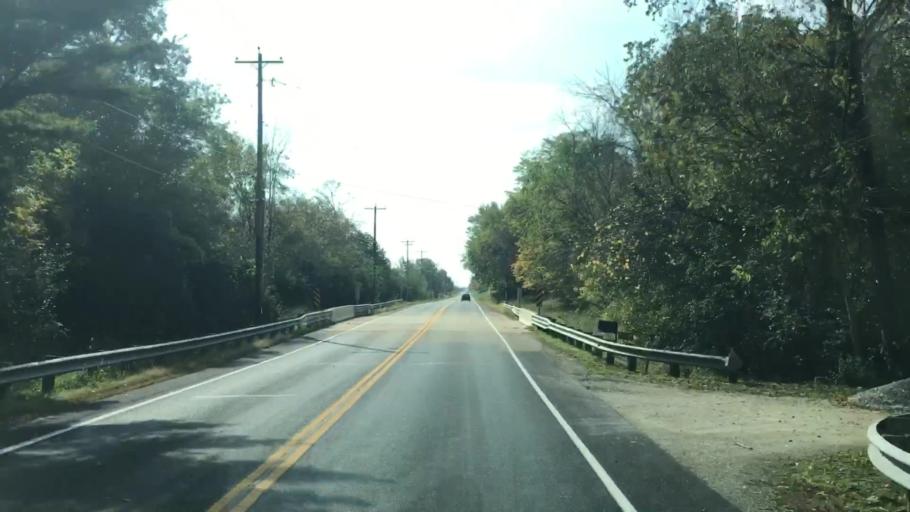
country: US
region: Wisconsin
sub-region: Ozaukee County
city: Mequon
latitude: 43.2189
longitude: -88.0435
